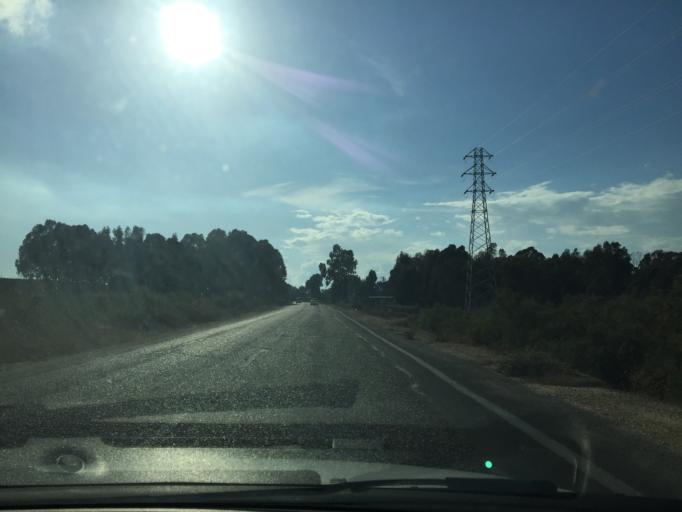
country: TR
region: Izmir
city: Selcuk
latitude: 37.9491
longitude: 27.2873
